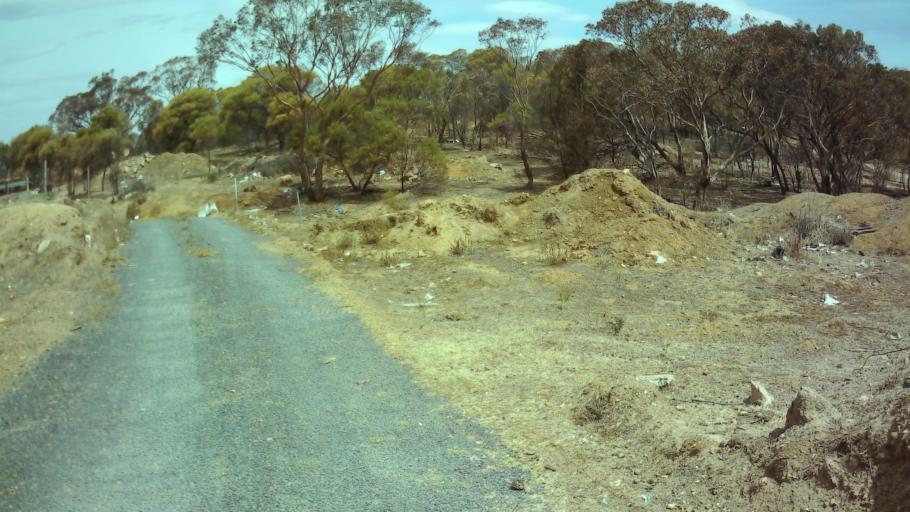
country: AU
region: New South Wales
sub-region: Weddin
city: Grenfell
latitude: -33.8695
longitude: 148.1643
